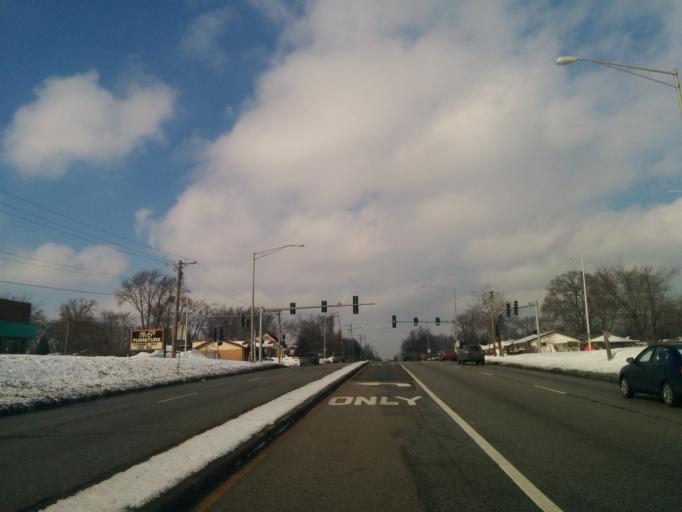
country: US
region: Illinois
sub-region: Cook County
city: Tinley Park
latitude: 41.5724
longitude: -87.7932
